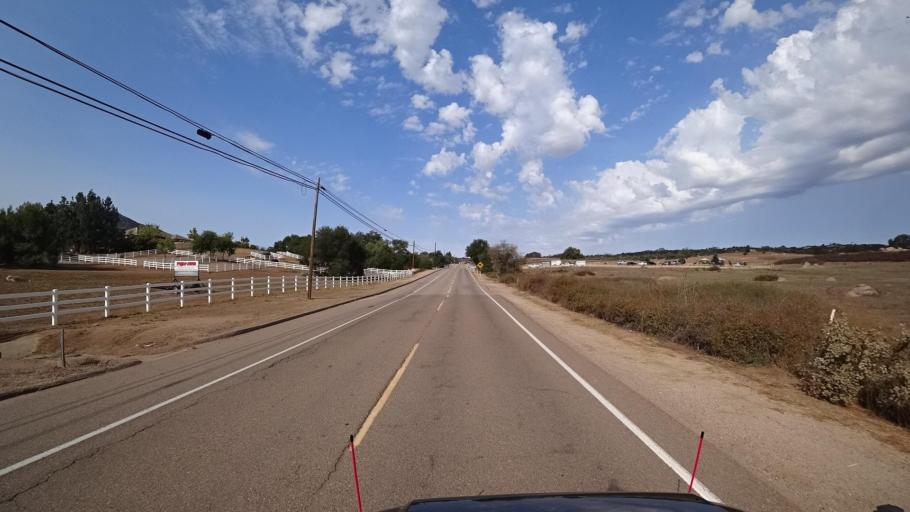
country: US
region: California
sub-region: San Diego County
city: San Pasqual
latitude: 33.0331
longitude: -116.9485
